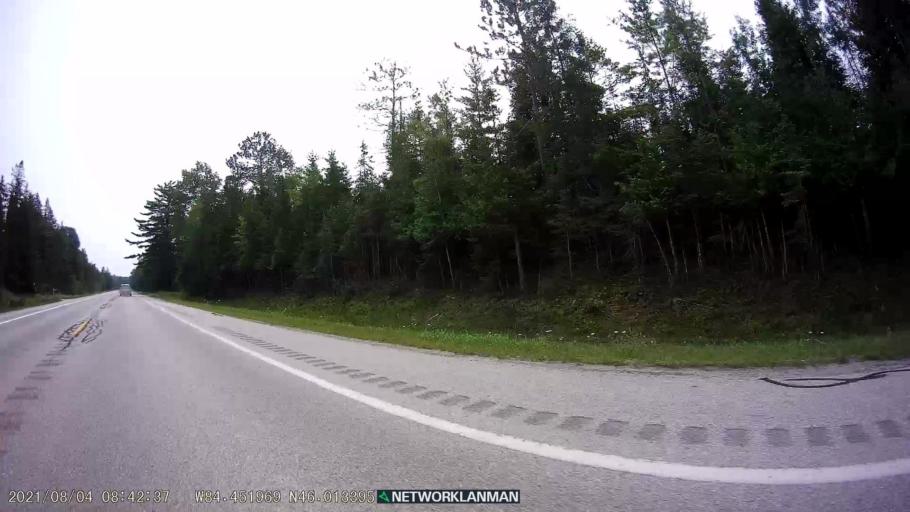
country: US
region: Michigan
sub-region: Mackinac County
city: Saint Ignace
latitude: 46.0134
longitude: -84.4496
